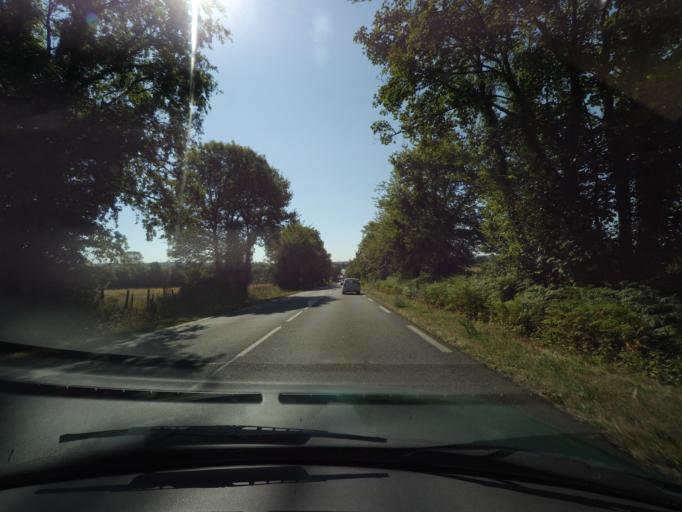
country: FR
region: Limousin
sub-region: Departement de la Haute-Vienne
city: Bussiere-Poitevine
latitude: 46.1738
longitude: 0.9475
